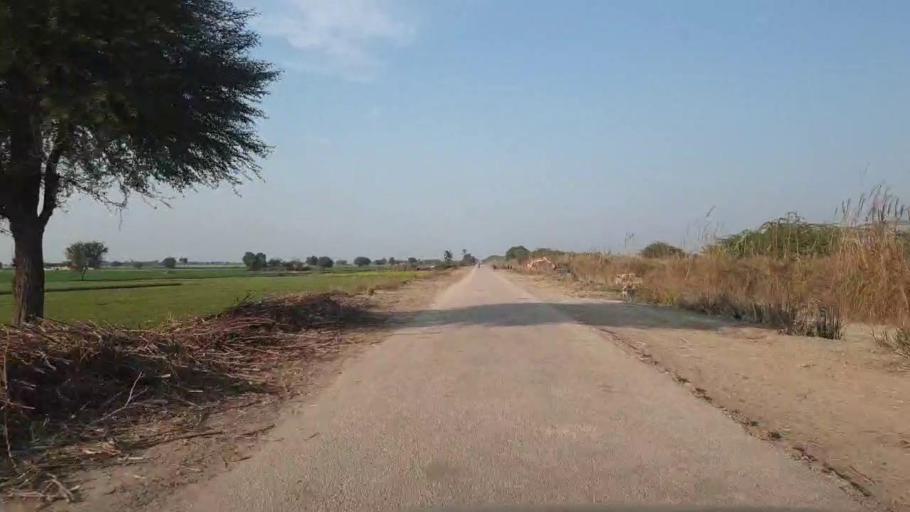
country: PK
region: Sindh
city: Shahpur Chakar
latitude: 26.1599
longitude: 68.6406
